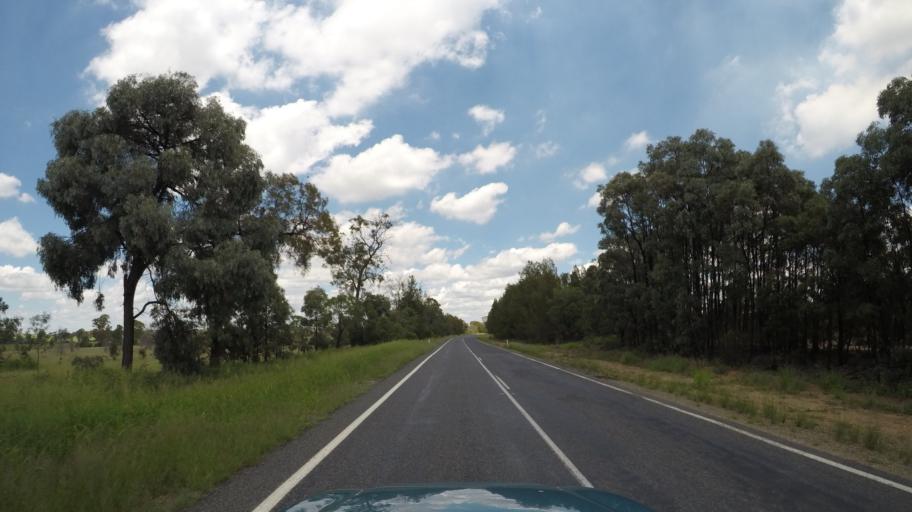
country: AU
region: Queensland
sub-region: Toowoomba
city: Oakey
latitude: -27.9497
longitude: 151.1432
